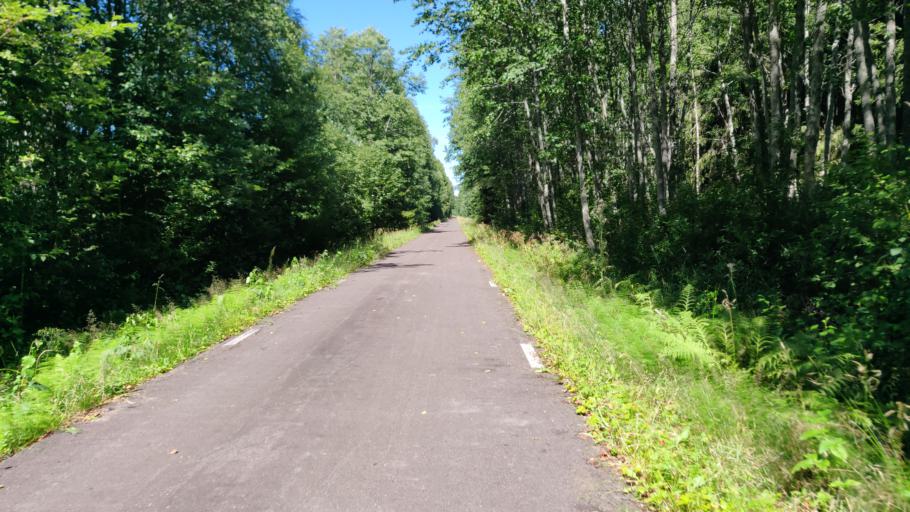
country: SE
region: Vaermland
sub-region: Hagfors Kommun
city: Hagfors
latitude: 59.9788
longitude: 13.5753
